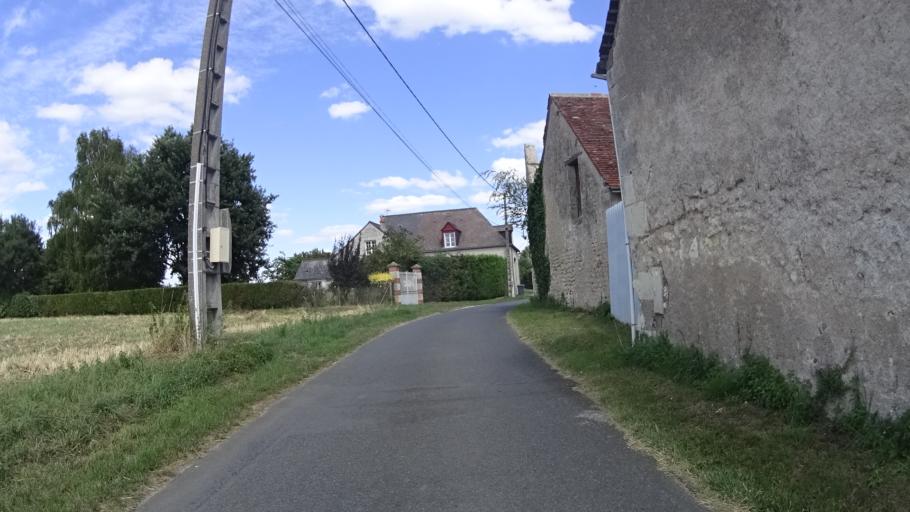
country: FR
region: Centre
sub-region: Departement d'Indre-et-Loire
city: Noizay
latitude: 47.4032
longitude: 0.8743
